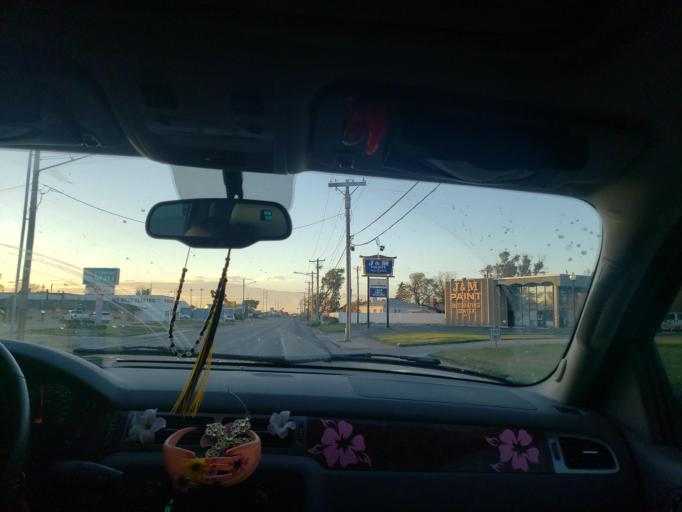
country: US
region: Kansas
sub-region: Finney County
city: Garden City
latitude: 37.9769
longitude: -100.8884
